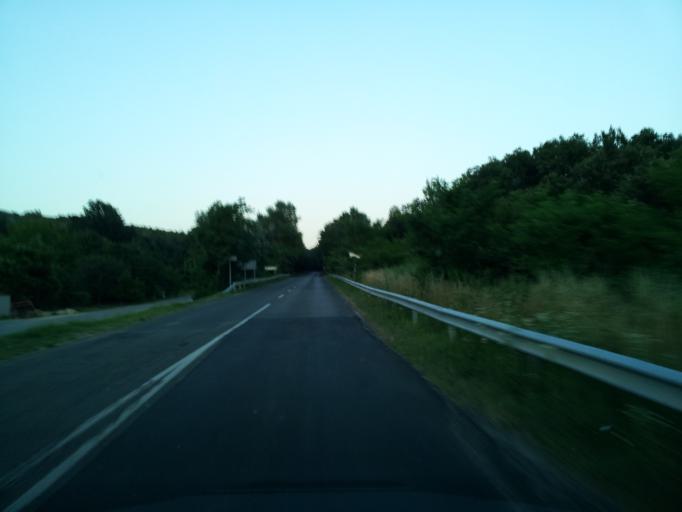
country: HU
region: Fejer
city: Szarliget
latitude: 47.5245
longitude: 18.4954
